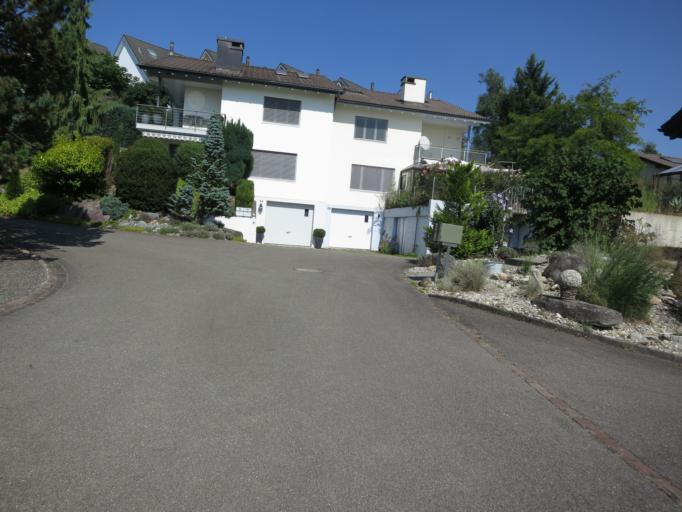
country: CH
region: Zurich
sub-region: Bezirk Hinwil
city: Wolfhausen
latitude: 47.2587
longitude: 8.7918
